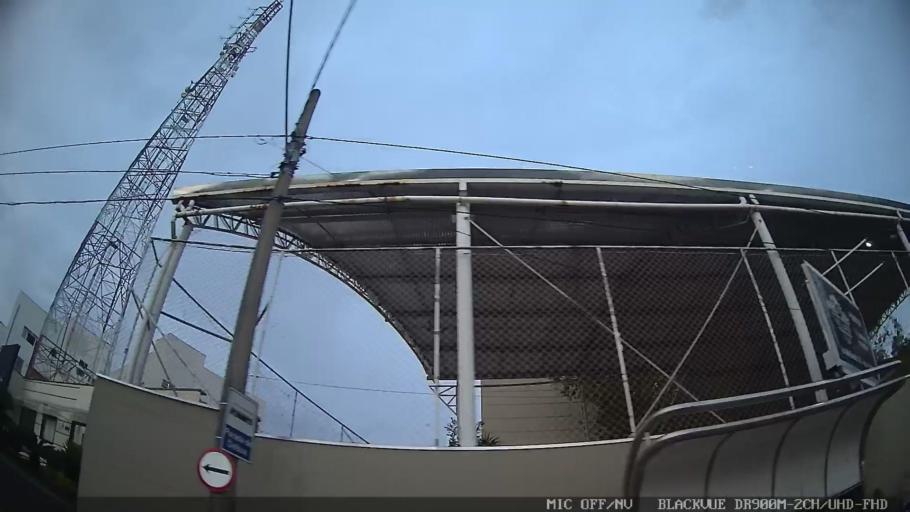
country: BR
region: Sao Paulo
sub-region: Vinhedo
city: Vinhedo
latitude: -23.0373
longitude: -46.9842
